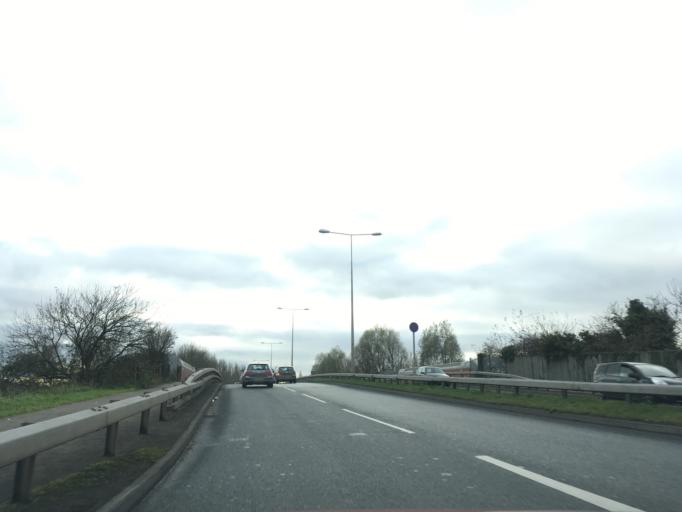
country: GB
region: Wales
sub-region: Newport
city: Caerleon
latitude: 51.5836
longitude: -2.9440
